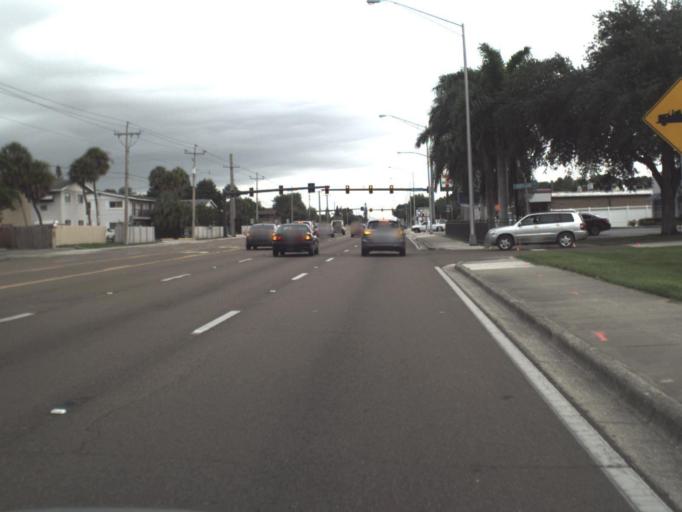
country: US
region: Florida
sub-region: Sarasota County
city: Southgate
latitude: 27.2987
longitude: -82.5094
